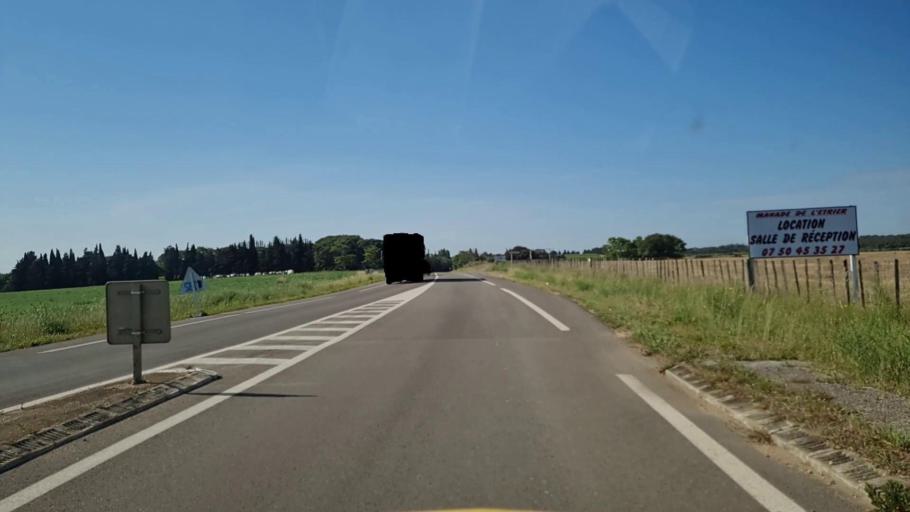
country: FR
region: Languedoc-Roussillon
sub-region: Departement du Gard
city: Garons
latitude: 43.7397
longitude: 4.4089
